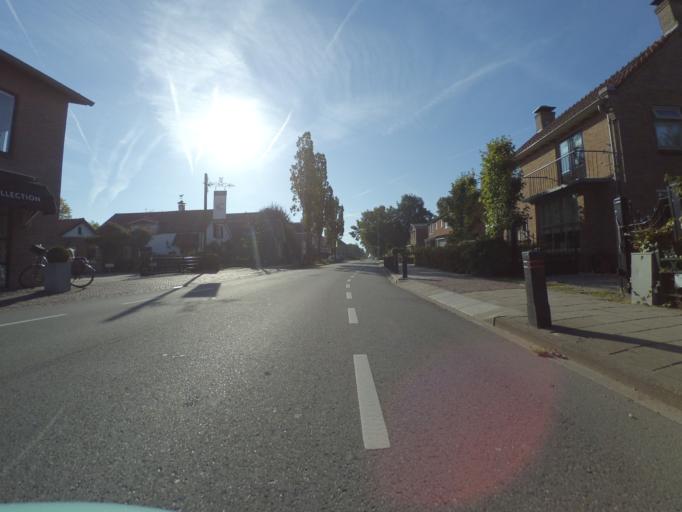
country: NL
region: Gelderland
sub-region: Gemeente Wageningen
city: Wageningen
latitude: 51.9331
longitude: 5.6337
